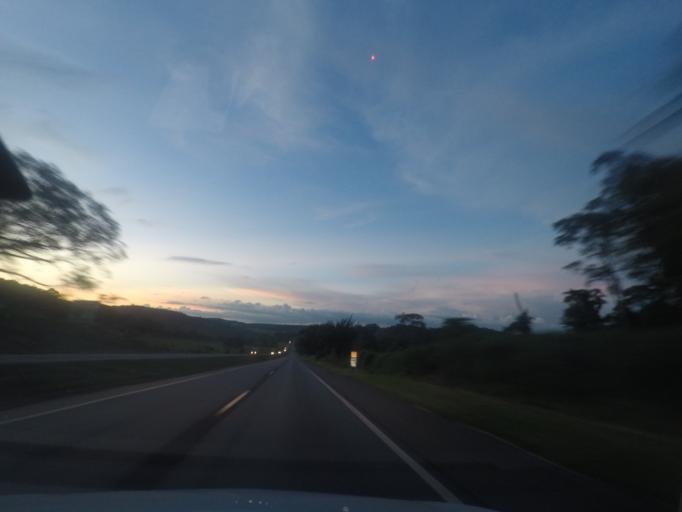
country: BR
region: Goias
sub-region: Pontalina
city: Pontalina
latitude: -17.4596
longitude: -49.2222
